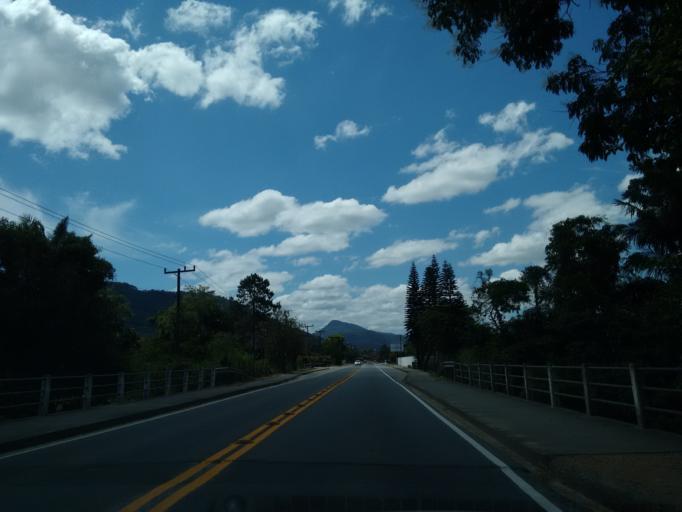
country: BR
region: Santa Catarina
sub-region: Pomerode
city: Pomerode
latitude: -26.7625
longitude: -49.1698
